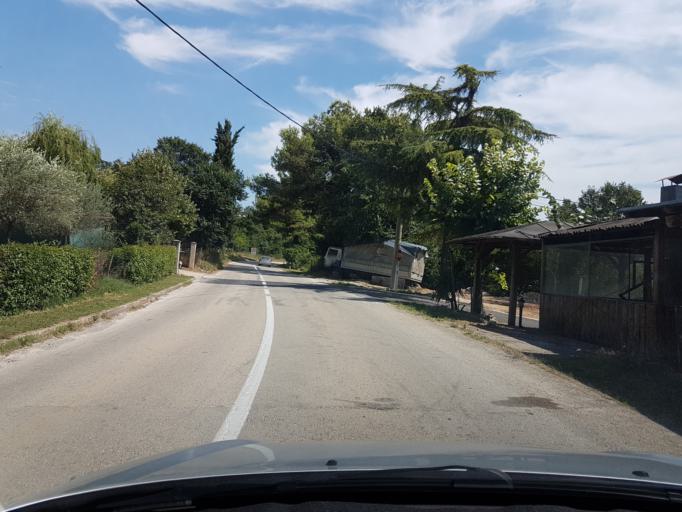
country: HR
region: Istarska
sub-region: Grad Rovinj
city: Rovinj
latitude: 45.1440
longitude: 13.7028
